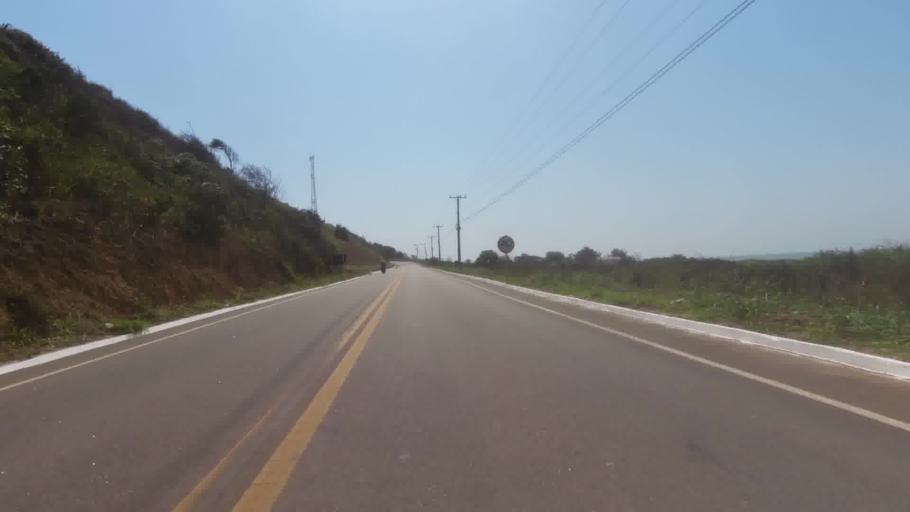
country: BR
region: Espirito Santo
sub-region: Marataizes
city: Marataizes
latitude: -21.0958
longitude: -40.8477
